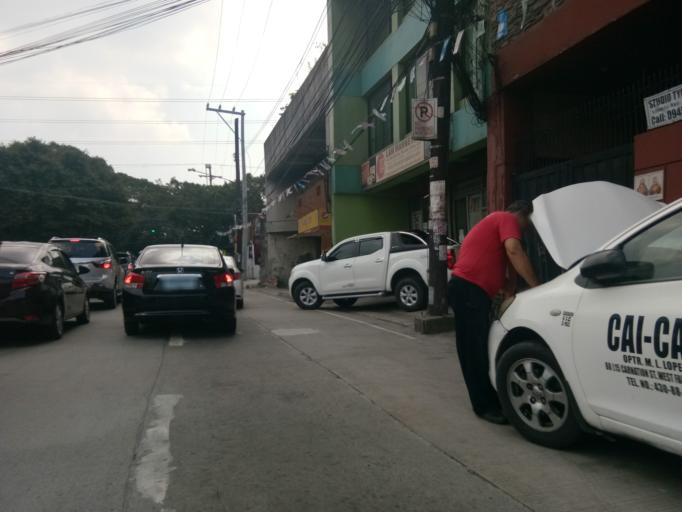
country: PH
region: Metro Manila
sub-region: Marikina
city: Calumpang
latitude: 14.6142
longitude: 121.0659
